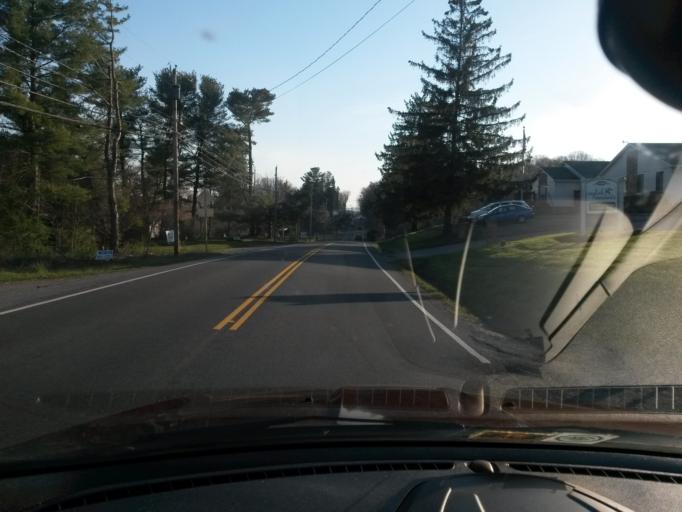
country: US
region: Virginia
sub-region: Montgomery County
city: Christiansburg
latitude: 37.1195
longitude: -80.4205
